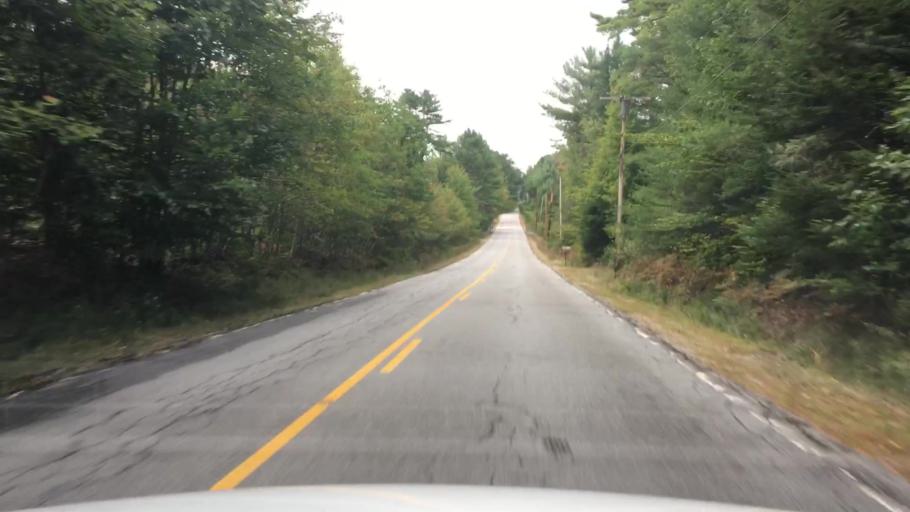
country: US
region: Maine
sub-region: York County
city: Parsonsfield
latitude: 43.7044
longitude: -70.9818
